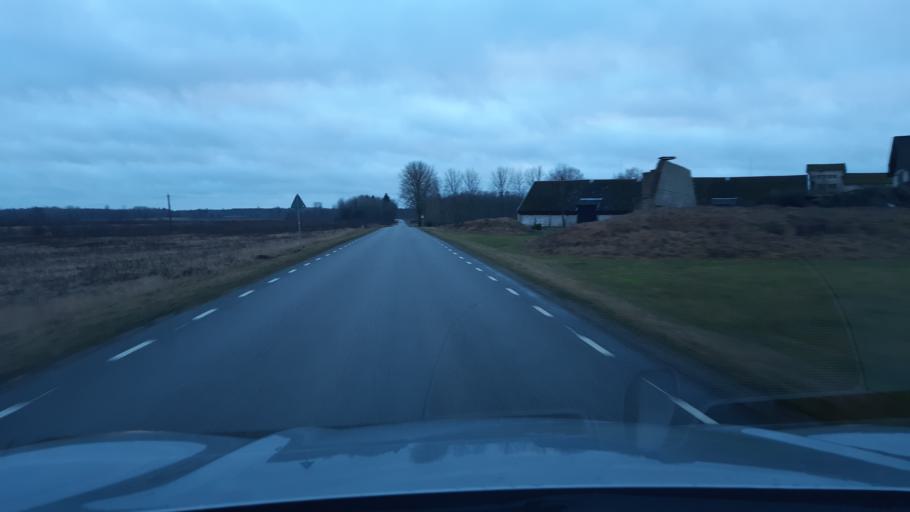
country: EE
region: Raplamaa
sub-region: Rapla vald
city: Rapla
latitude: 59.0438
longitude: 24.6767
